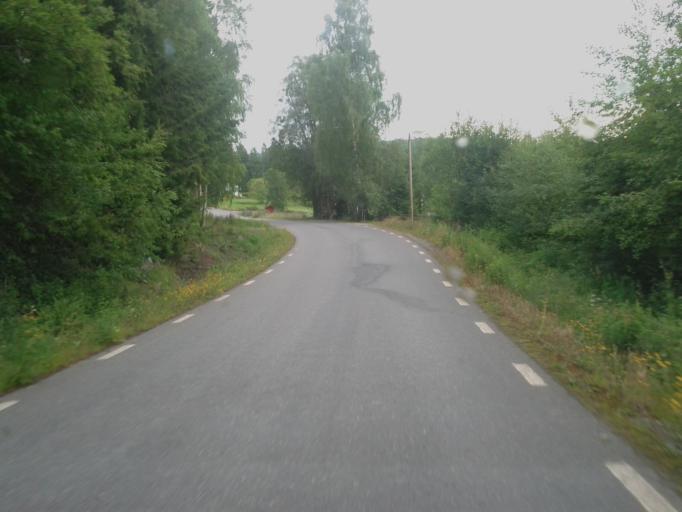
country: SE
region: Vaesternorrland
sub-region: Kramfors Kommun
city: Nordingra
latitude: 63.0614
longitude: 18.4075
